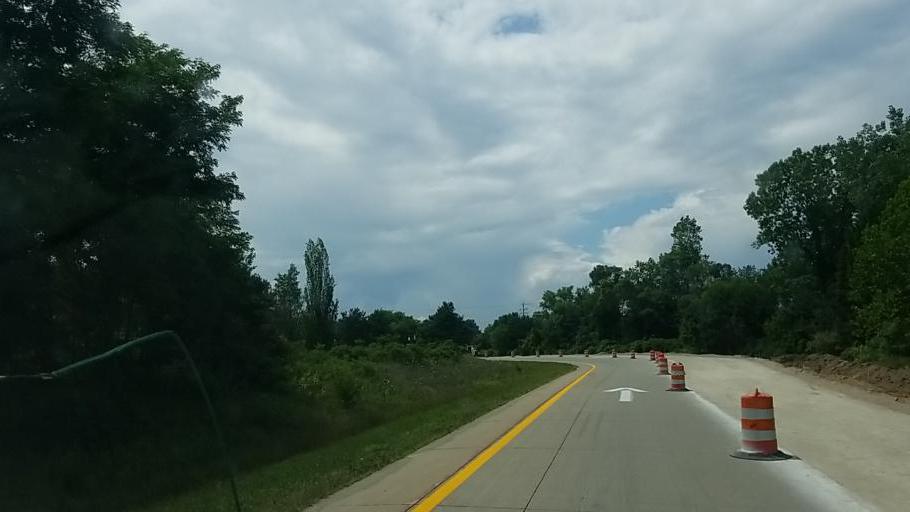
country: US
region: Michigan
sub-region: Kent County
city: Walker
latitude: 43.0226
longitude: -85.7239
